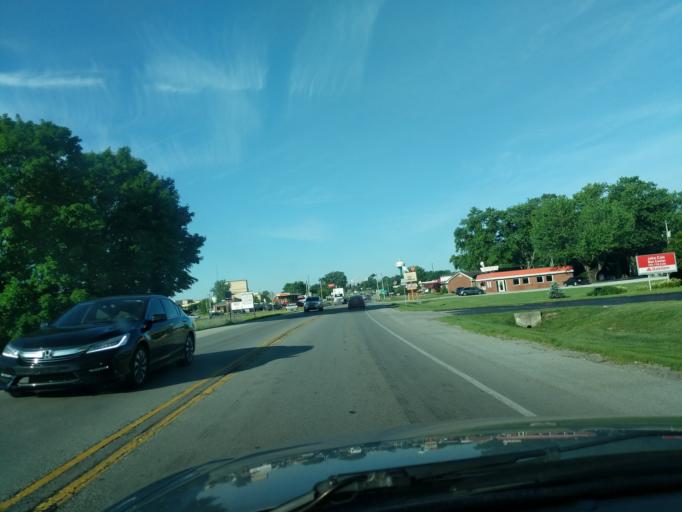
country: US
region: Indiana
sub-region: Madison County
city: Pendleton
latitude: 40.0030
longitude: -85.7315
